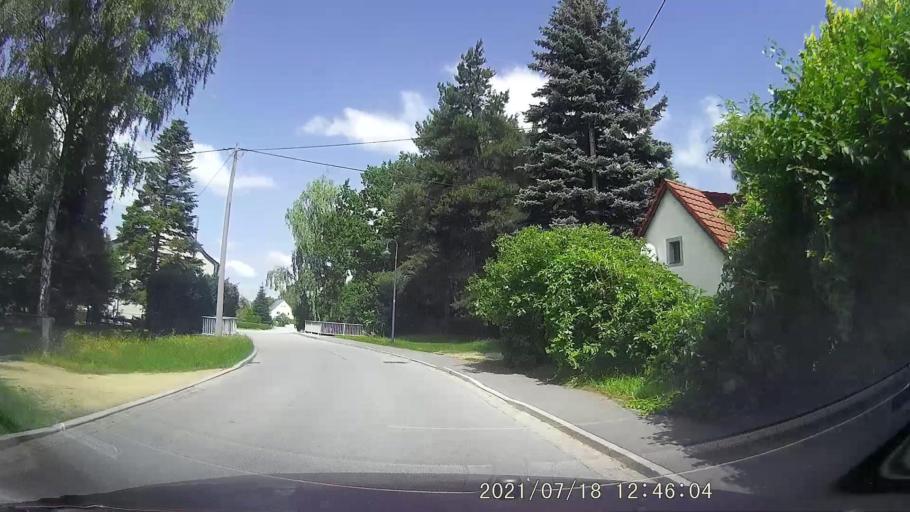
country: DE
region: Saxony
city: Reichenbach
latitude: 51.1901
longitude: 14.7897
